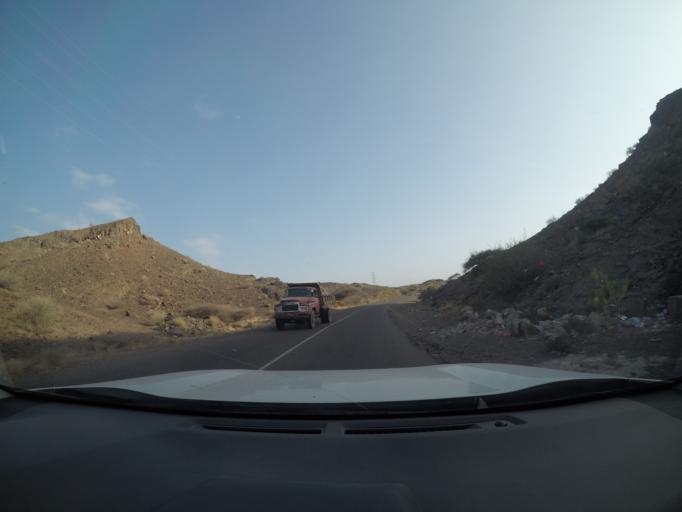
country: YE
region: Lahij
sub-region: Al Milah
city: Al Milah
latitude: 13.3826
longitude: 44.8101
